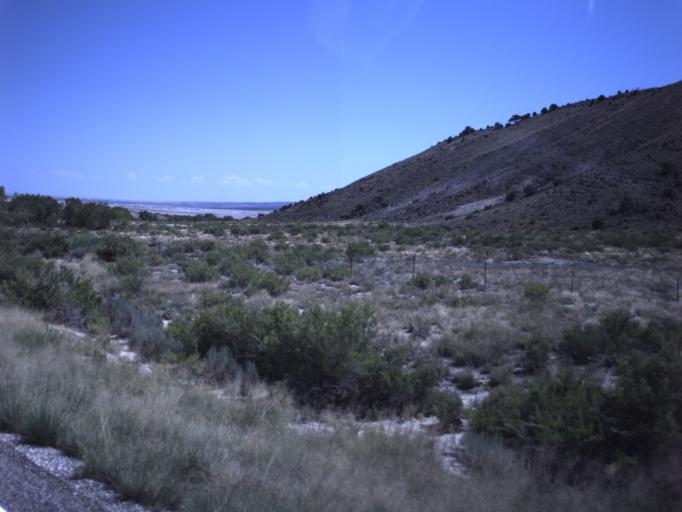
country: US
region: Utah
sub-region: Emery County
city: Ferron
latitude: 38.7878
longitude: -111.3498
